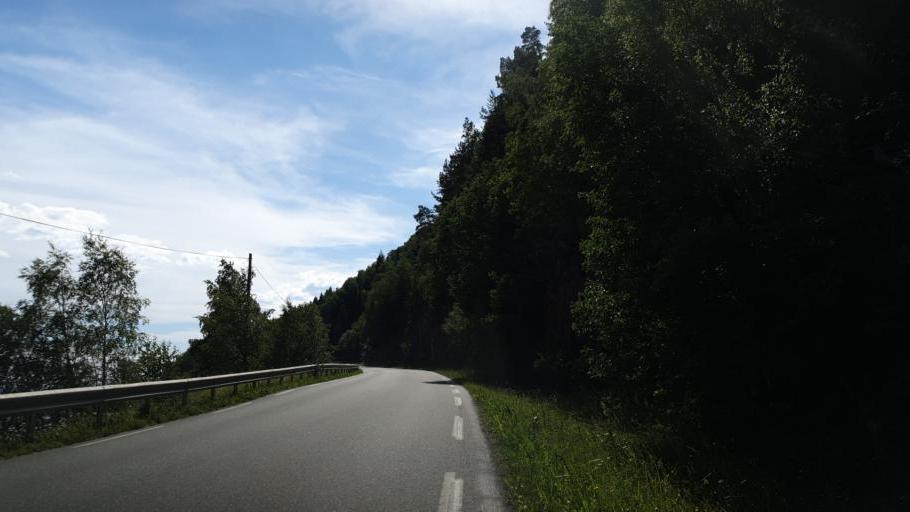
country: NO
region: Nord-Trondelag
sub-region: Leksvik
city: Leksvik
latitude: 63.6390
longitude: 10.5847
